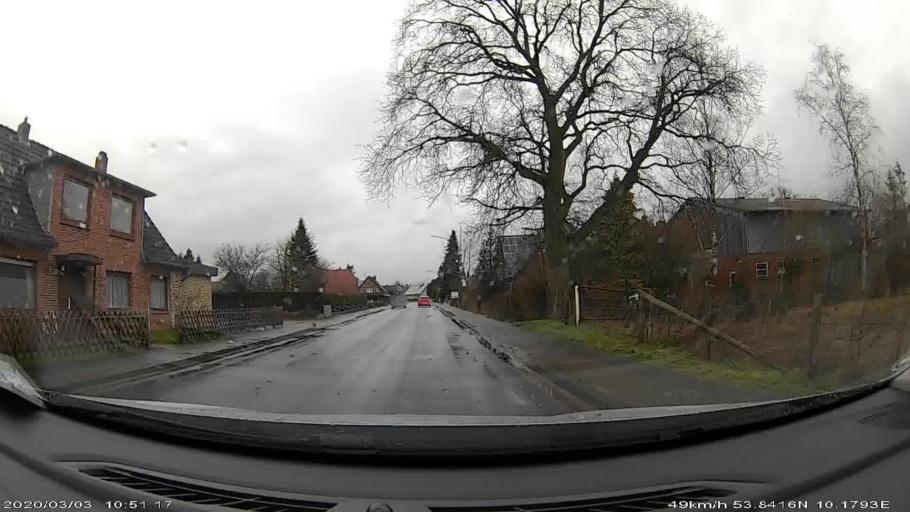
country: DE
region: Schleswig-Holstein
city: Seth
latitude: 53.8434
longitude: 10.1772
